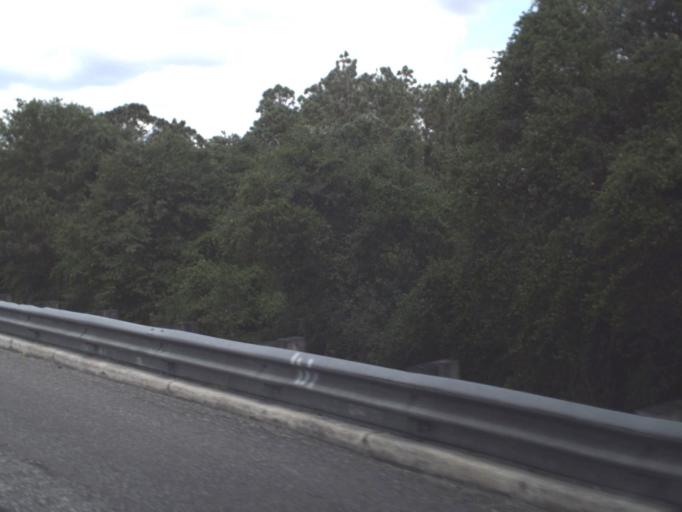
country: US
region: Florida
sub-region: Orange County
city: Wedgefield
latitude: 28.4525
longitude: -81.0256
